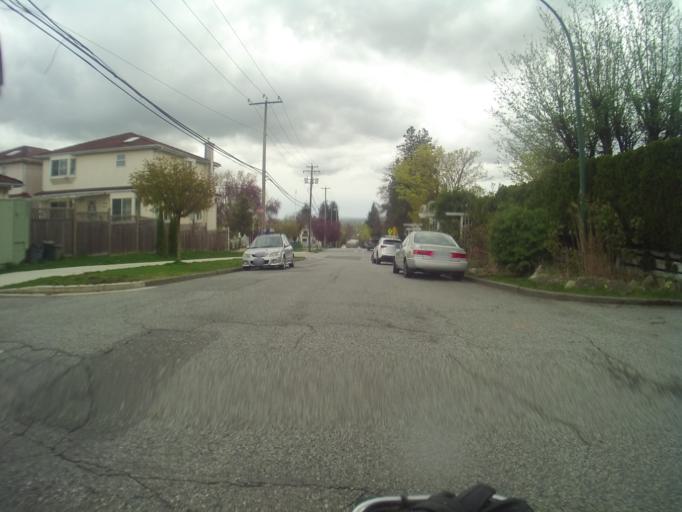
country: CA
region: British Columbia
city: Vancouver
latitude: 49.2159
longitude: -123.0740
